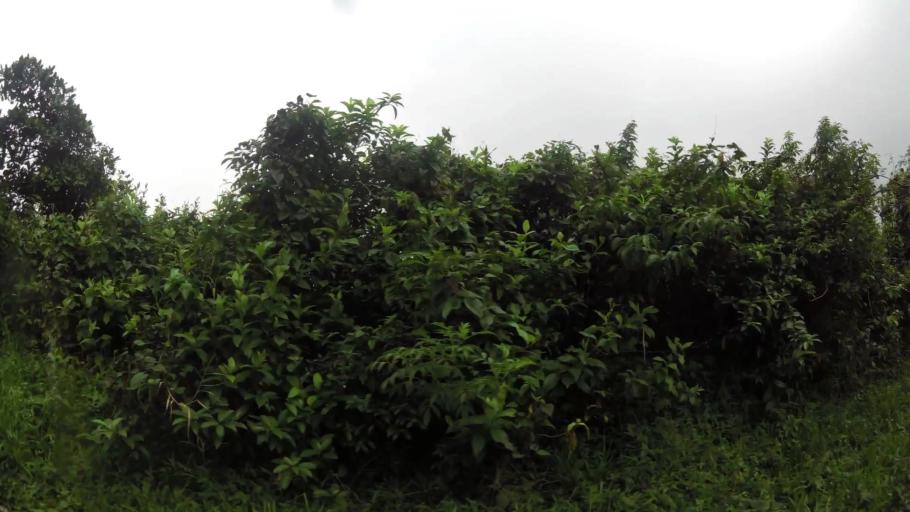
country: MQ
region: Martinique
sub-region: Martinique
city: Le Morne-Rouge
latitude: 14.8062
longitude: -61.1493
